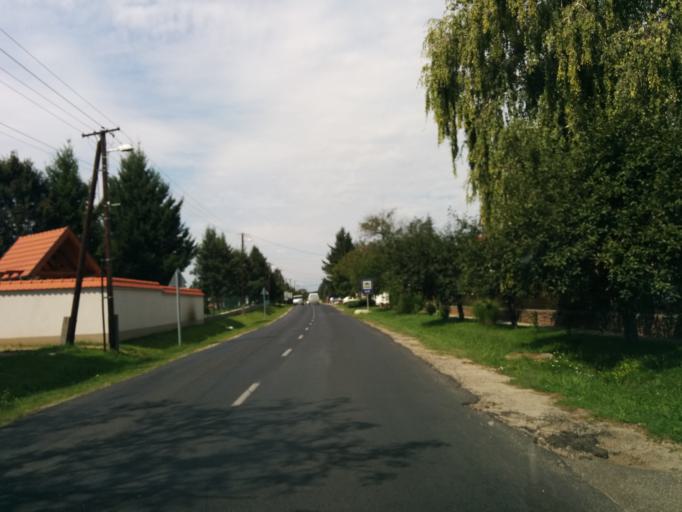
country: HU
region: Gyor-Moson-Sopron
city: Fertod
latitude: 47.6156
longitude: 16.8338
